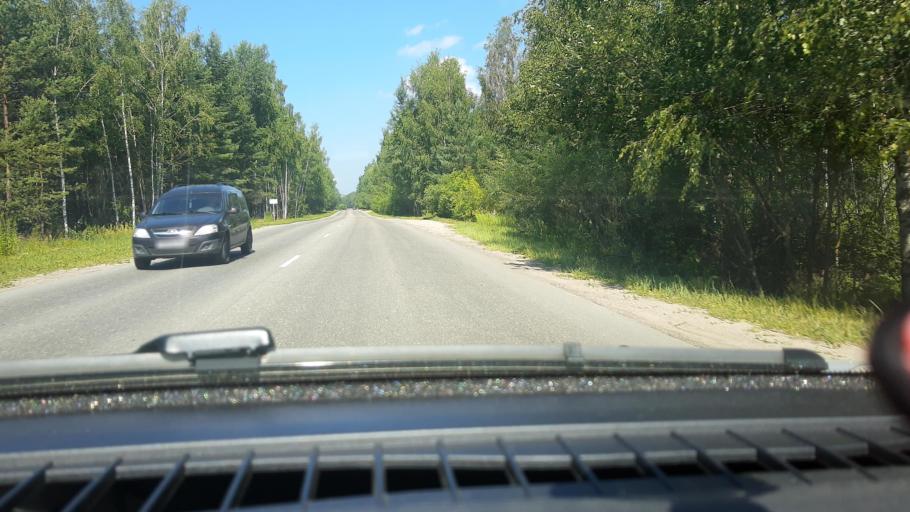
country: RU
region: Nizjnij Novgorod
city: Afonino
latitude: 56.3101
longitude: 44.1721
